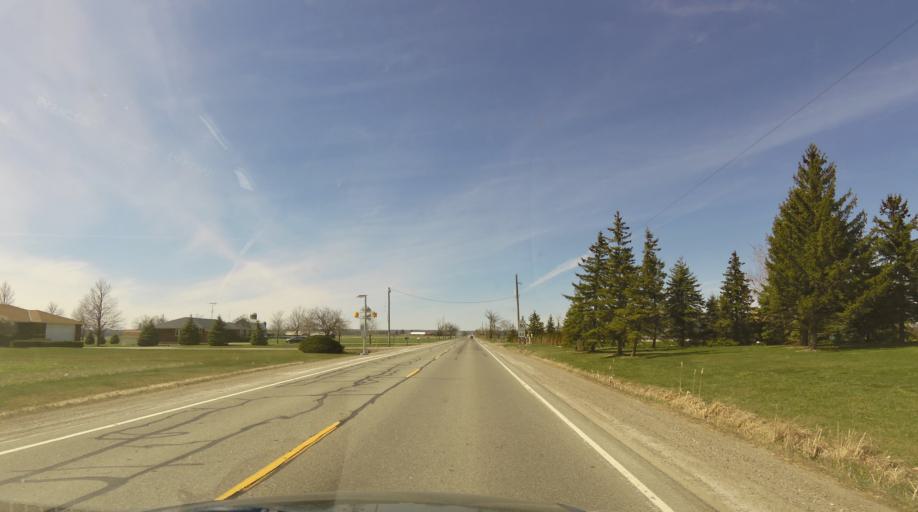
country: CA
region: Ontario
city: Brampton
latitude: 43.7016
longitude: -79.8767
